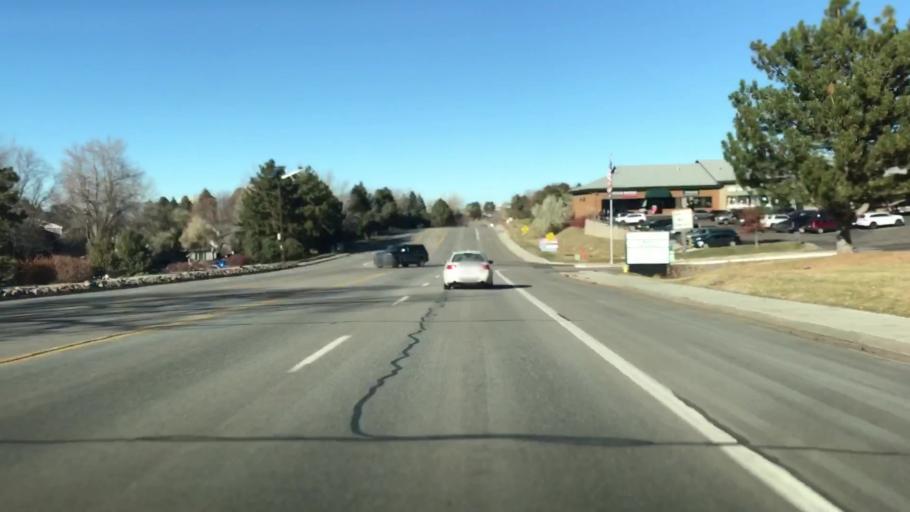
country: US
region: Colorado
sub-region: Arapahoe County
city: Centennial
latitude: 39.5837
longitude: -104.8855
